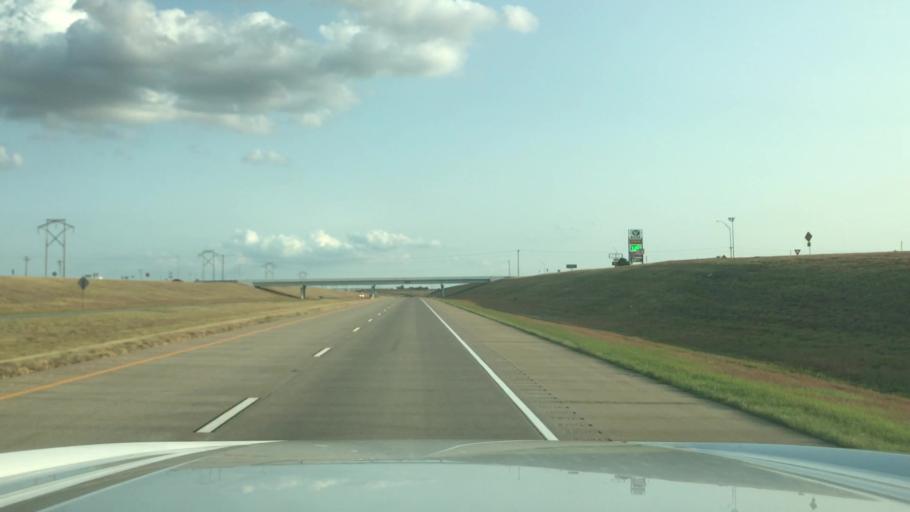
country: US
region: Texas
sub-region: Swisher County
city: Tulia
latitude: 34.5324
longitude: -101.7956
